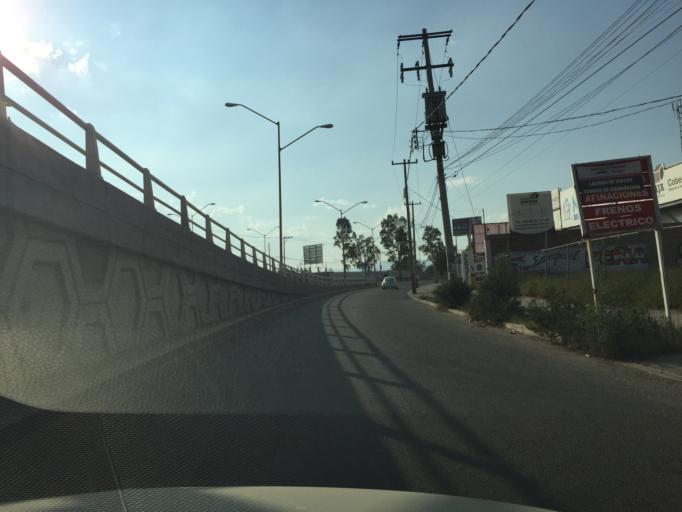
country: MX
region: Aguascalientes
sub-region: Aguascalientes
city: La Loma de los Negritos
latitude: 21.8595
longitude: -102.3151
